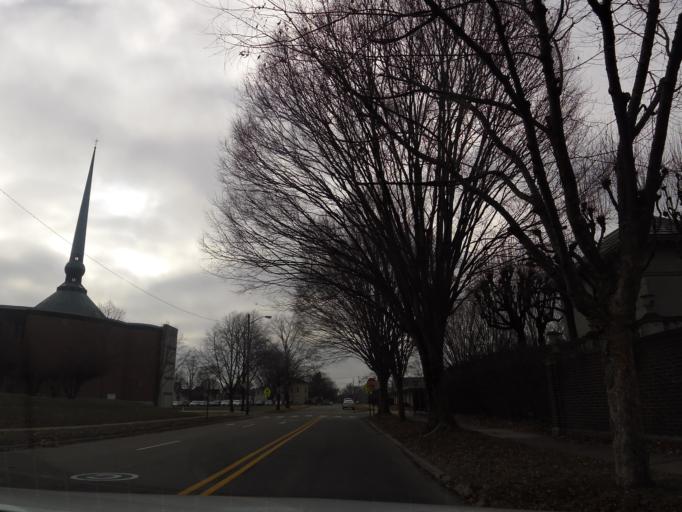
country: US
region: Indiana
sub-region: Bartholomew County
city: Columbus
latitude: 39.2041
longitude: -85.9172
